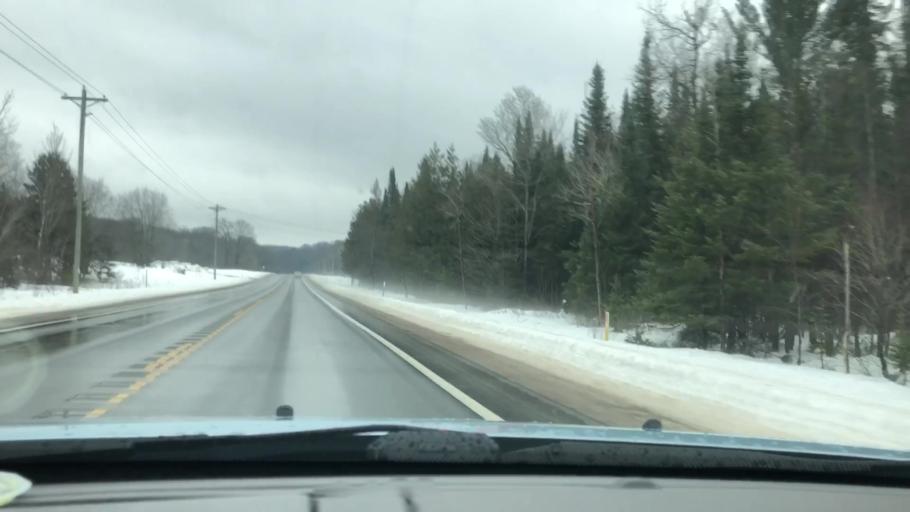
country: US
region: Michigan
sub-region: Charlevoix County
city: Boyne City
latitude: 45.0901
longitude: -84.9451
